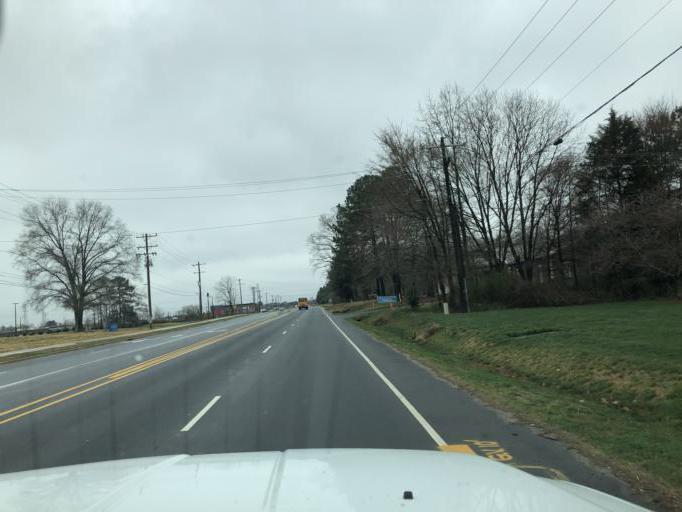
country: US
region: North Carolina
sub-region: Gaston County
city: Mount Holly
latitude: 35.3314
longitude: -80.9394
